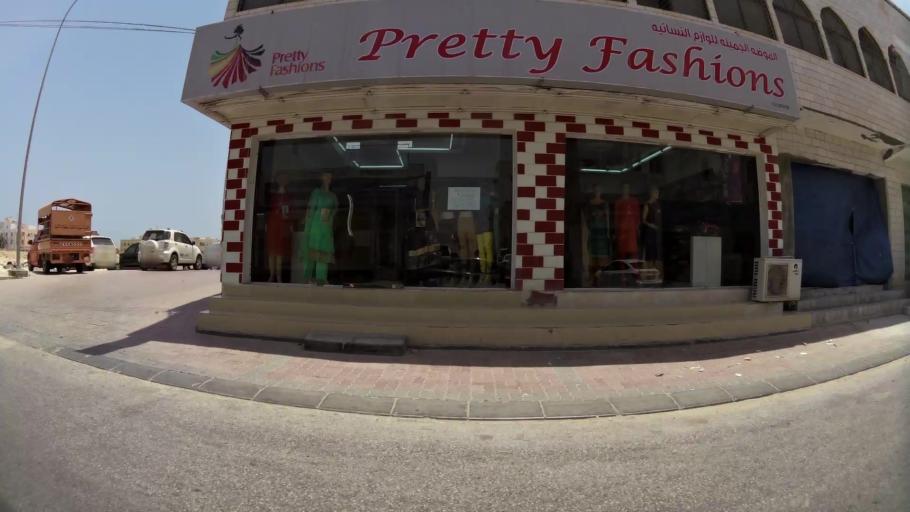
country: OM
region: Zufar
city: Salalah
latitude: 17.0167
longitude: 54.1012
